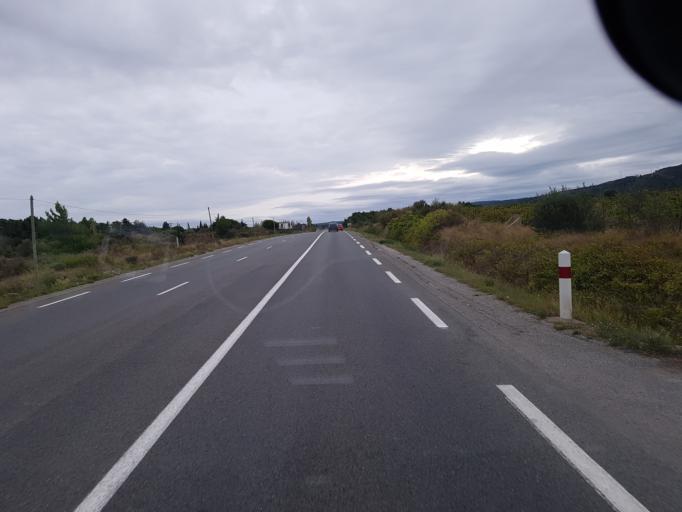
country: FR
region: Languedoc-Roussillon
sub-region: Departement de l'Aude
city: Peyriac-de-Mer
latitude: 43.1325
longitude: 2.9645
